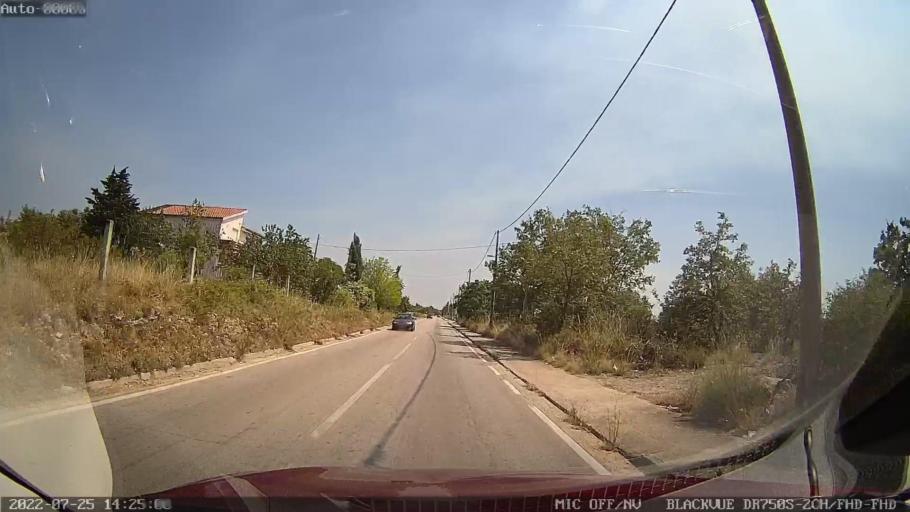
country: HR
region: Zadarska
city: Policnik
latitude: 44.1465
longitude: 15.3286
